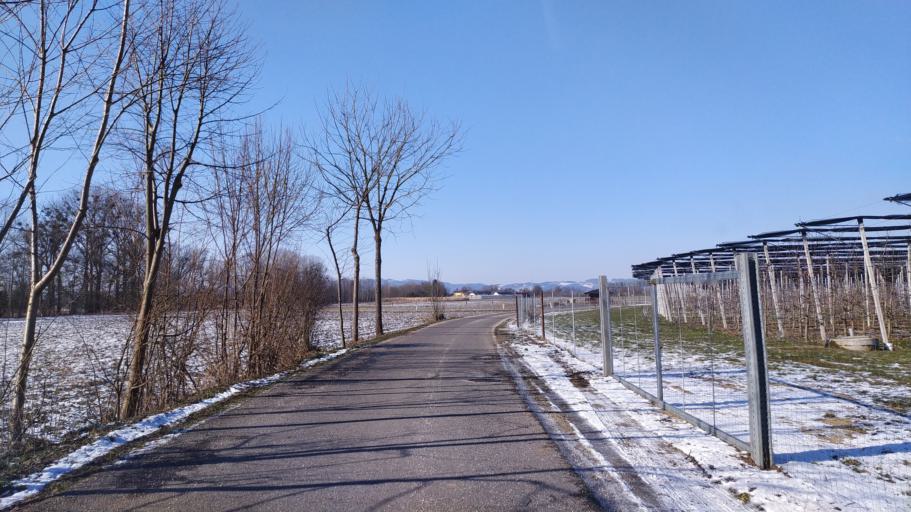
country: AT
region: Upper Austria
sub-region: Politischer Bezirk Urfahr-Umgebung
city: Goldworth
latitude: 48.3315
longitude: 14.0907
